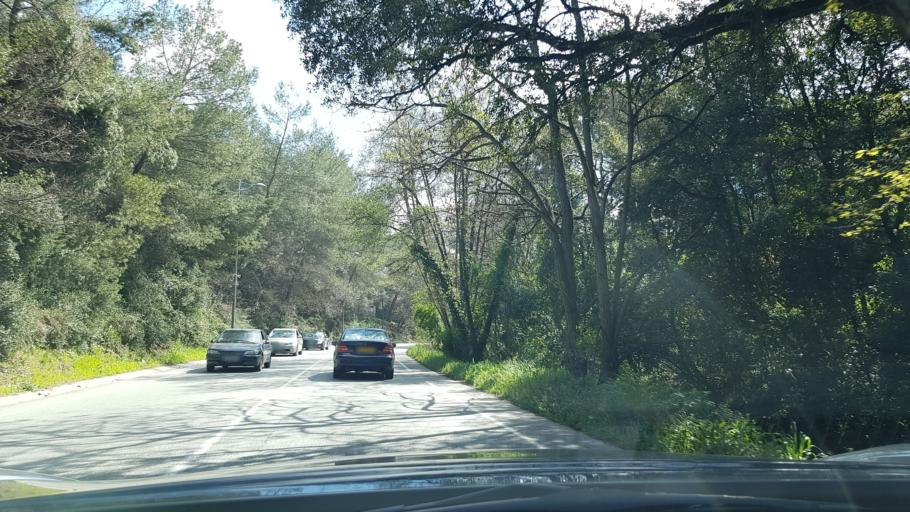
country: FR
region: Provence-Alpes-Cote d'Azur
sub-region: Departement des Alpes-Maritimes
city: Vallauris
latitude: 43.5987
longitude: 7.0576
